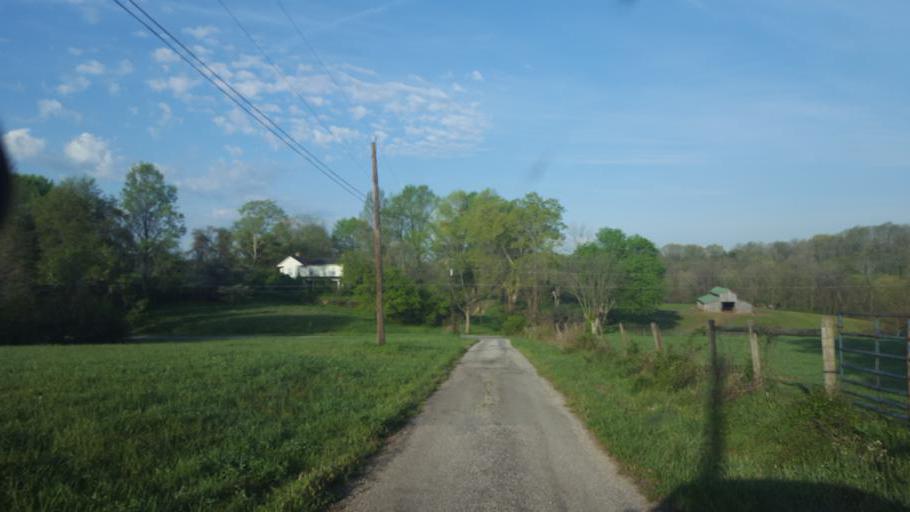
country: US
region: Kentucky
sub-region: Hart County
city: Munfordville
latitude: 37.2636
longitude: -85.8874
